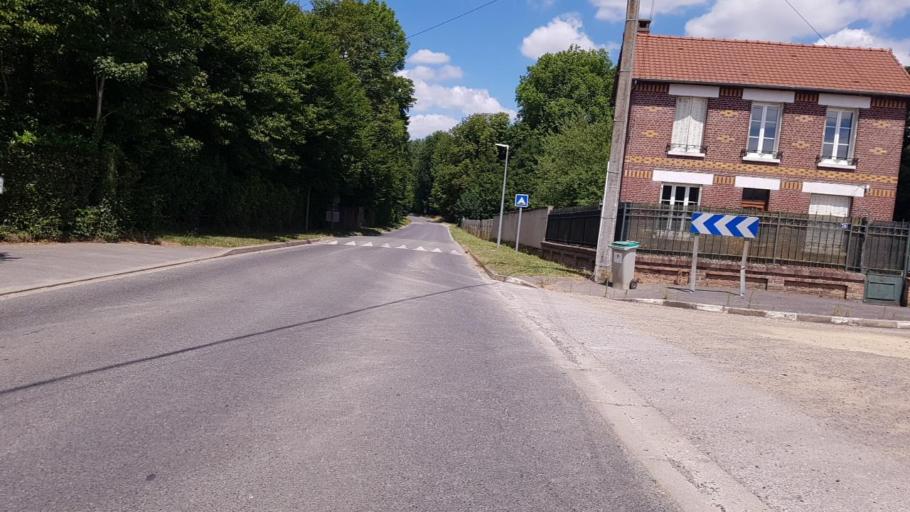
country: FR
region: Picardie
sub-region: Departement de l'Oise
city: Tracy-le-Mont
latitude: 49.5035
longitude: 2.9804
